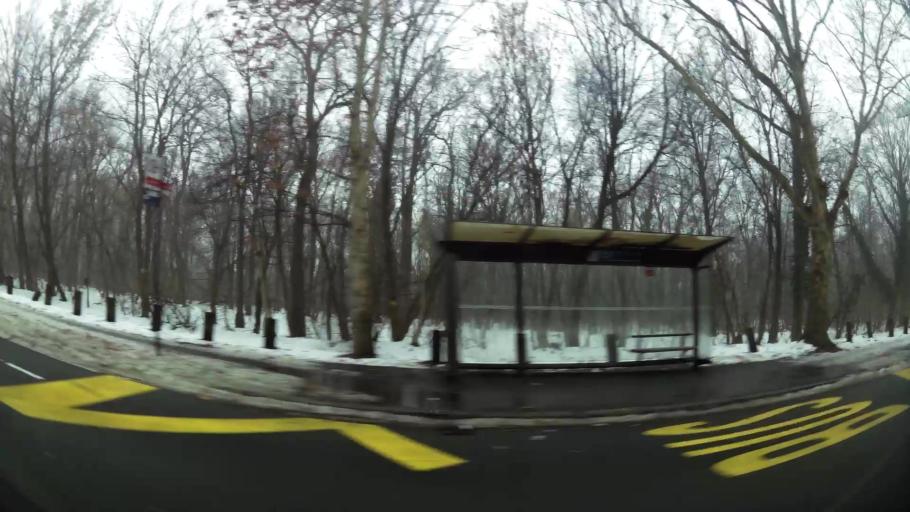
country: RS
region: Central Serbia
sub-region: Belgrade
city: Vozdovac
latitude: 44.7653
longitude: 20.4780
